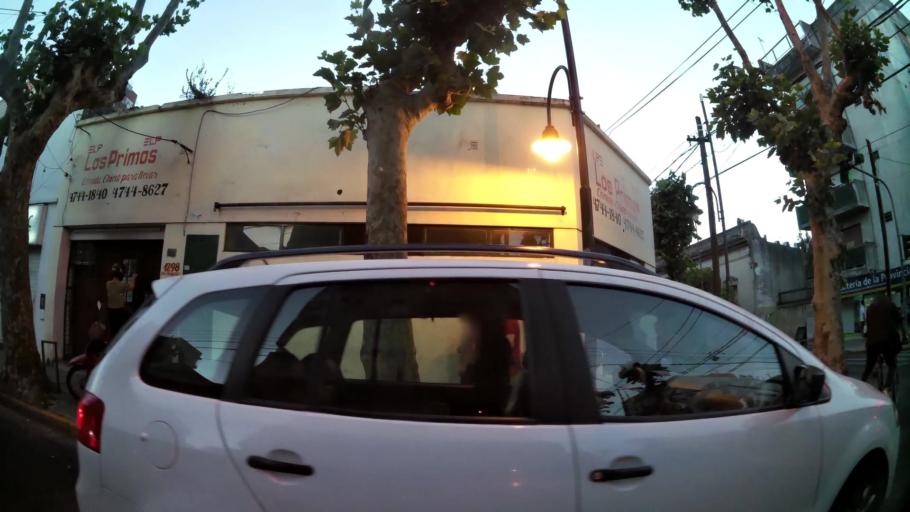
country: AR
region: Buenos Aires
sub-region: Partido de Tigre
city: Tigre
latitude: -34.4430
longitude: -58.5558
